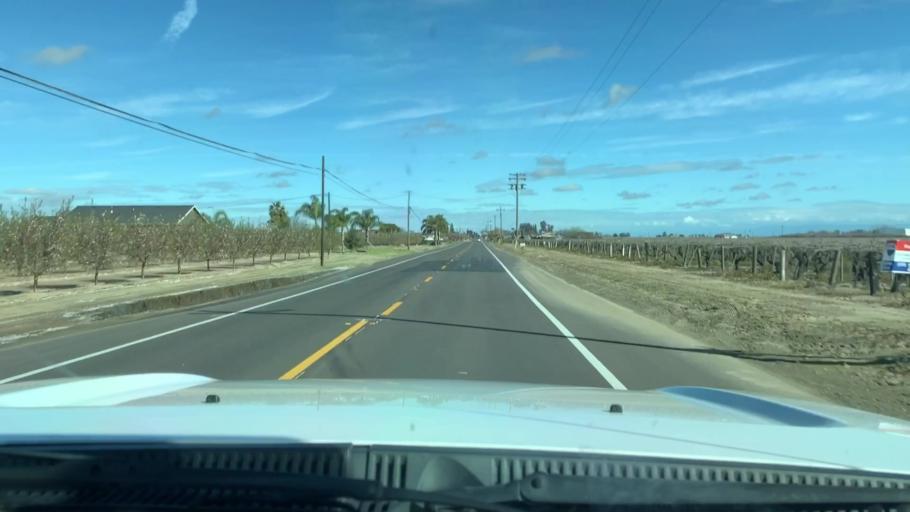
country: US
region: California
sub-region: Fresno County
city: Selma
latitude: 36.5372
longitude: -119.6828
